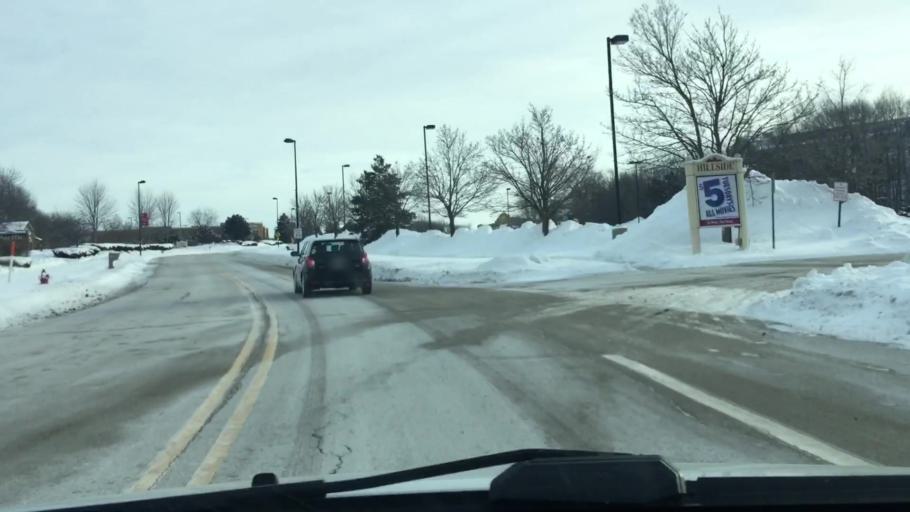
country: US
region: Wisconsin
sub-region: Waukesha County
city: Delafield
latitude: 43.0478
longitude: -88.3684
